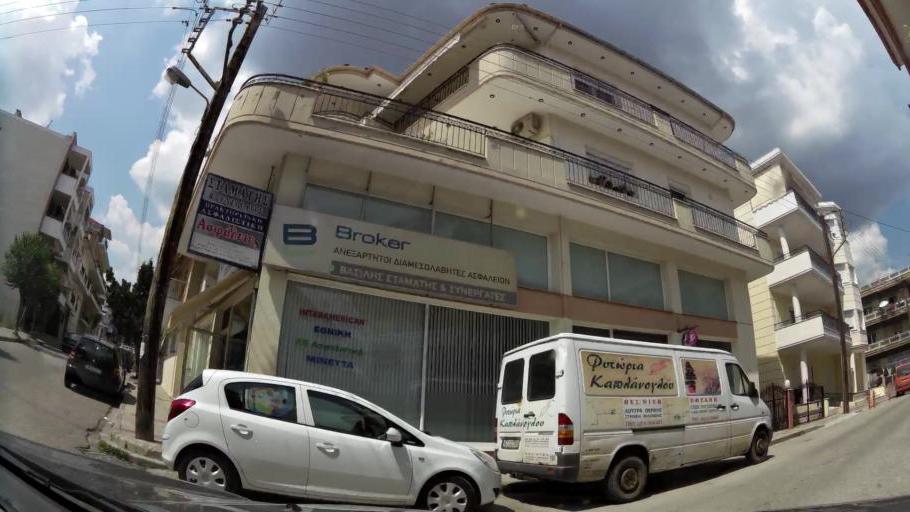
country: GR
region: West Macedonia
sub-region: Nomos Kozanis
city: Kozani
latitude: 40.3001
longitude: 21.7957
